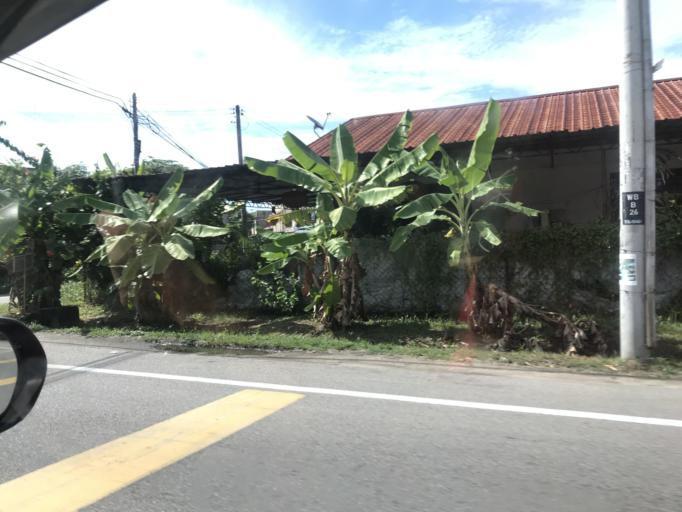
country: MY
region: Kelantan
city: Kota Bharu
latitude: 6.1192
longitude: 102.1987
